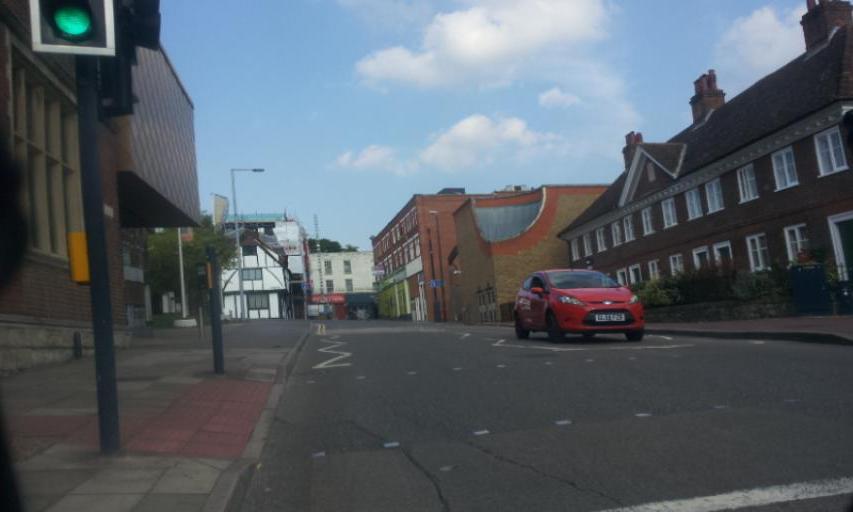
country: GB
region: England
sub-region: Kent
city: Maidstone
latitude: 51.2758
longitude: 0.5207
